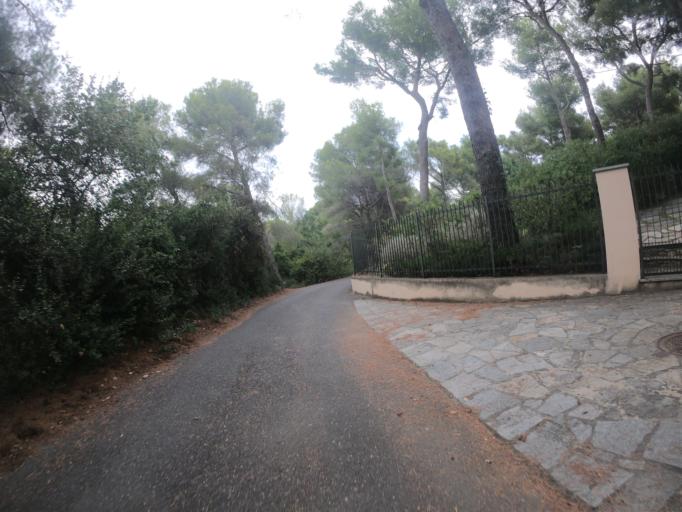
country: IT
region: Liguria
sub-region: Provincia di Savona
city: Marina di Andora
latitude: 43.9559
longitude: 8.1554
